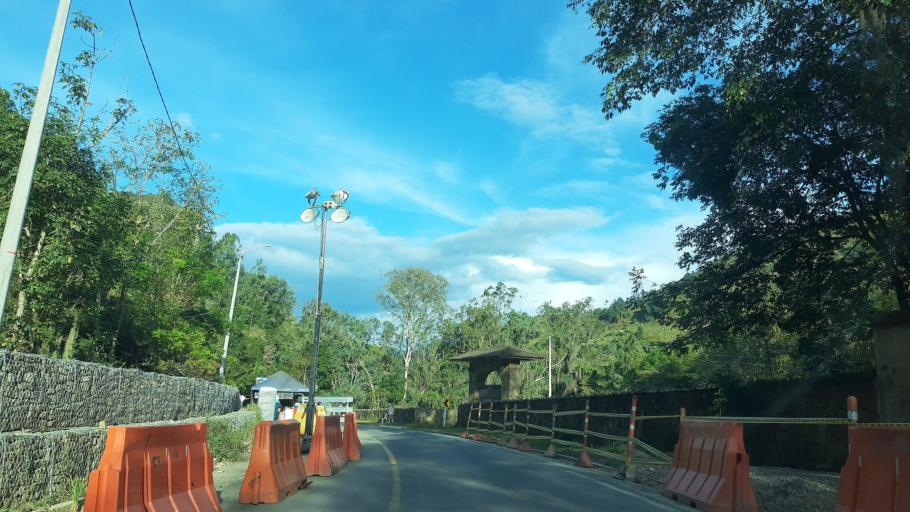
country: CO
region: Cundinamarca
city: Macheta
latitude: 5.0750
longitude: -73.5823
